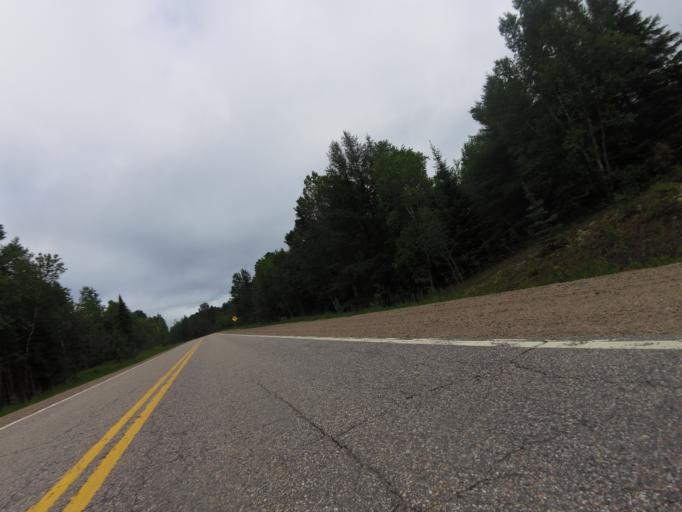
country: CA
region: Quebec
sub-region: Outaouais
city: Shawville
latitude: 45.9100
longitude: -76.3130
